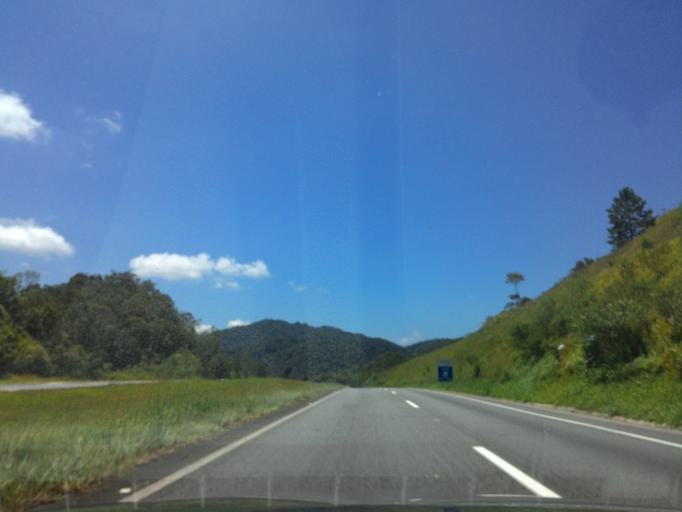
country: BR
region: Parana
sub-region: Antonina
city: Antonina
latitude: -25.0835
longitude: -48.6315
